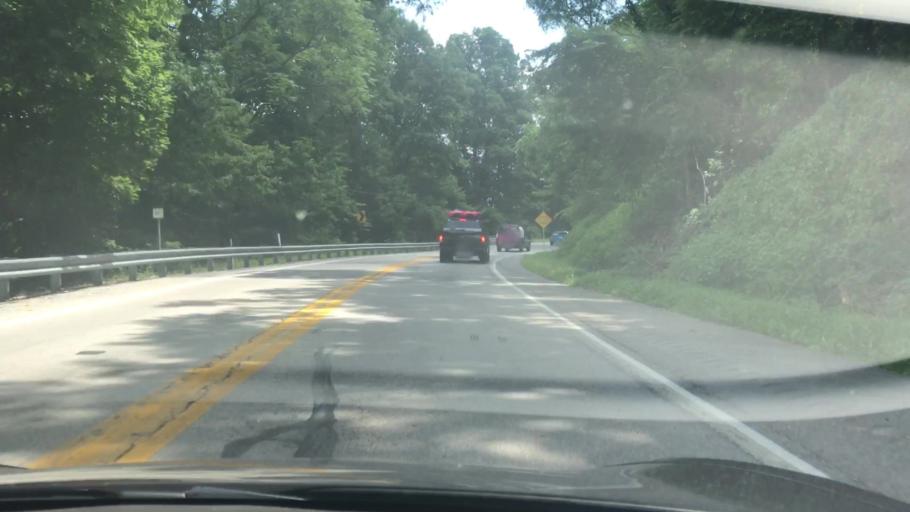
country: US
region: Pennsylvania
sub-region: York County
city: Manchester
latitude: 40.0981
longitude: -76.7615
